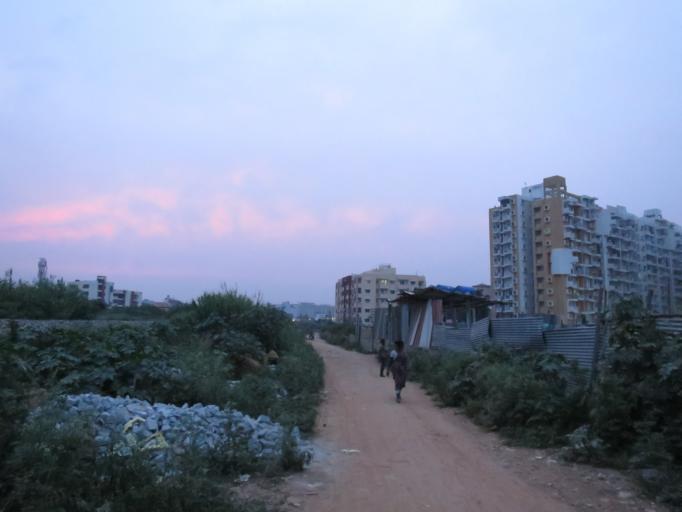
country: IN
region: Karnataka
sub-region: Bangalore Urban
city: Bangalore
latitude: 12.9717
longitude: 77.7007
